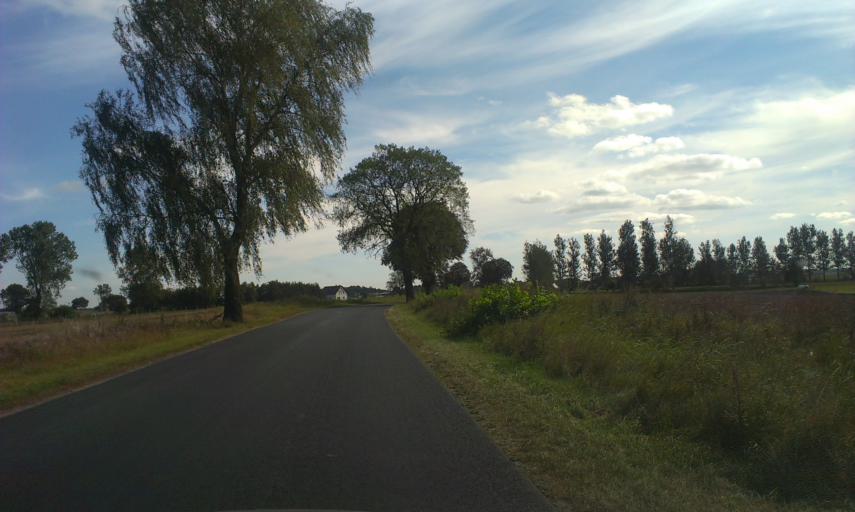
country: PL
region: Greater Poland Voivodeship
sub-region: Powiat zlotowski
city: Zlotow
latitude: 53.3127
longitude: 17.1207
